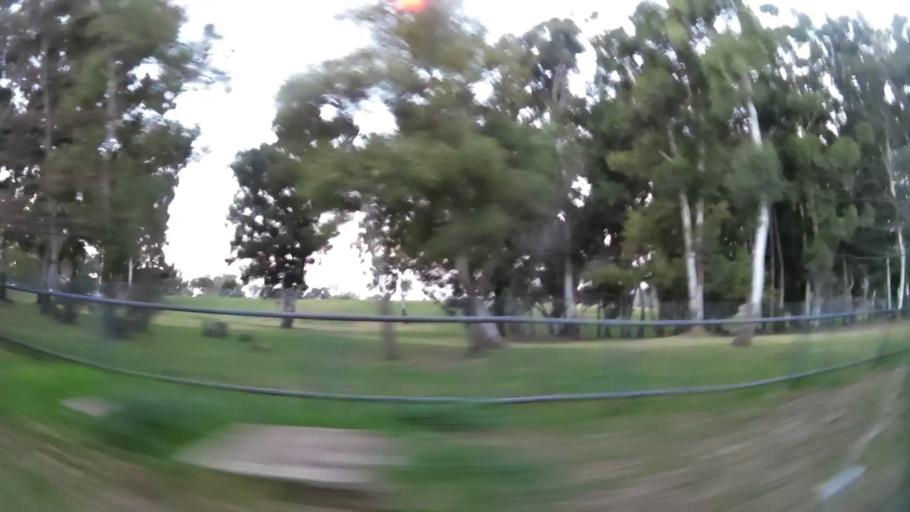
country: ZA
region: Gauteng
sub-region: City of Johannesburg Metropolitan Municipality
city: Johannesburg
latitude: -26.1387
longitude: 28.0591
